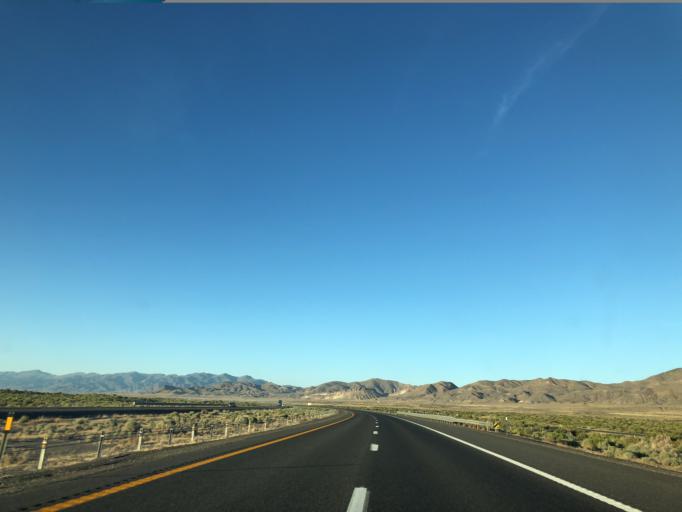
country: US
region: Nevada
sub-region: Pershing County
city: Lovelock
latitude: 40.1964
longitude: -118.4381
